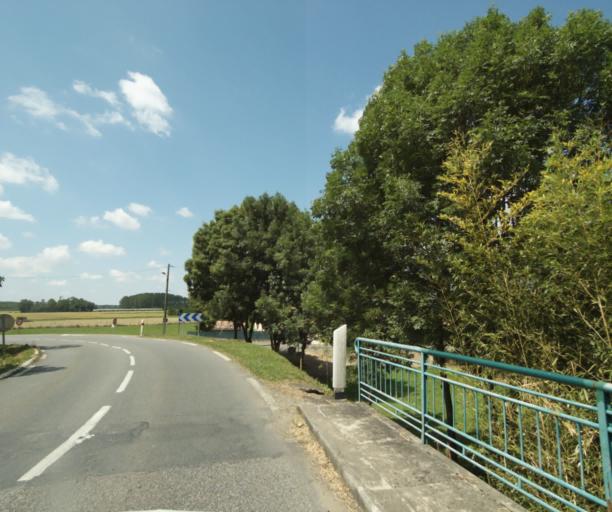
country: FR
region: Midi-Pyrenees
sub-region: Departement du Tarn-et-Garonne
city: Montauban
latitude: 44.0834
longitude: 1.3472
